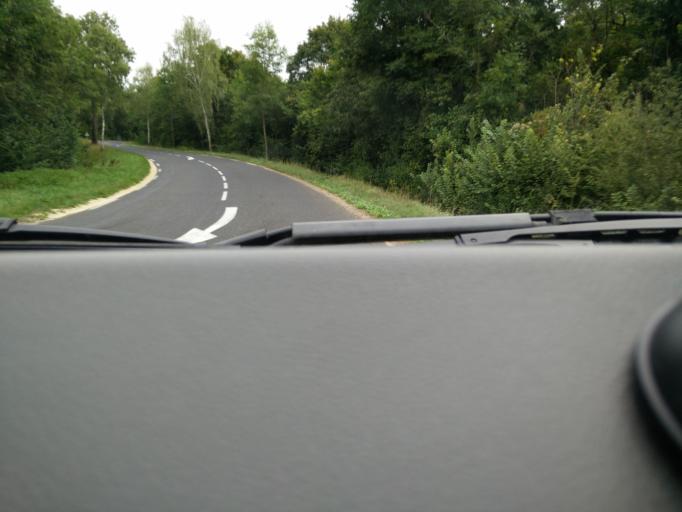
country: FR
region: Lorraine
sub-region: Departement de Meurthe-et-Moselle
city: Montauville
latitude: 48.9396
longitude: 5.8859
